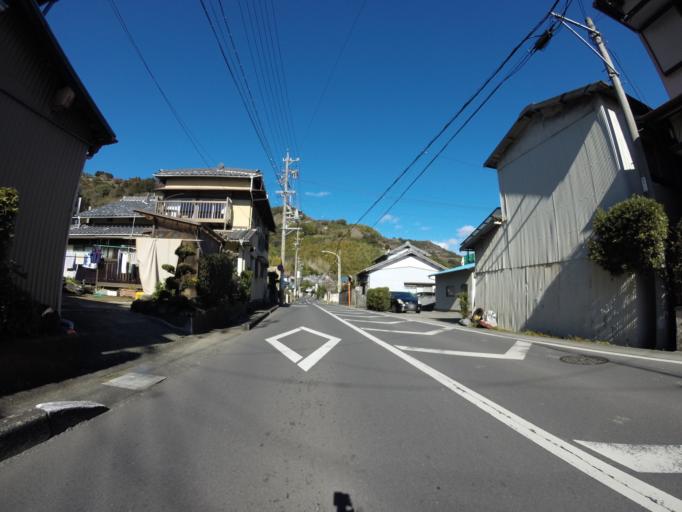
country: JP
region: Shizuoka
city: Shizuoka-shi
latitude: 35.0113
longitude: 138.3852
